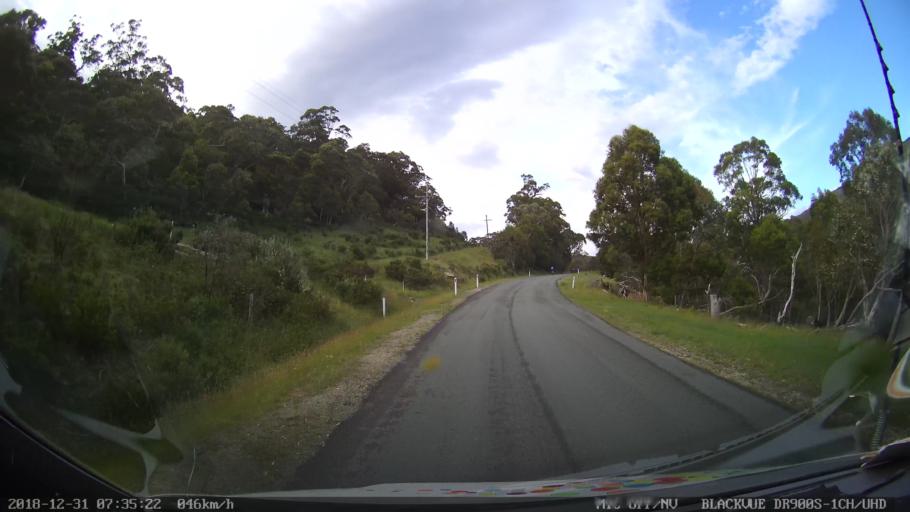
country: AU
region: New South Wales
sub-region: Snowy River
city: Jindabyne
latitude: -36.3346
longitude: 148.4451
